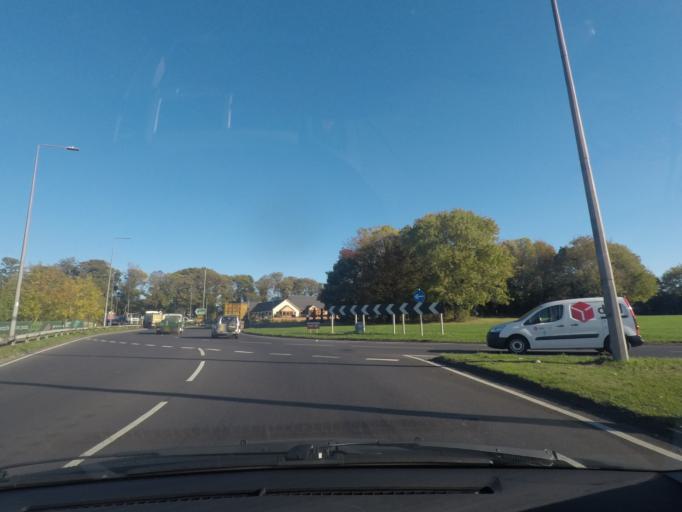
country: GB
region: England
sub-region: East Riding of Yorkshire
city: Hessle
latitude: 53.7247
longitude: -0.4583
